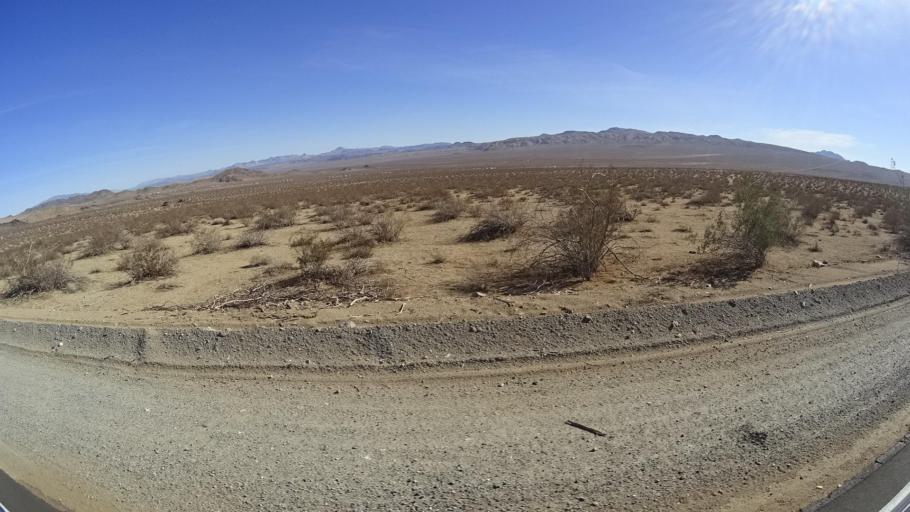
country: US
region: California
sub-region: Kern County
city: Ridgecrest
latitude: 35.5344
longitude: -117.5895
